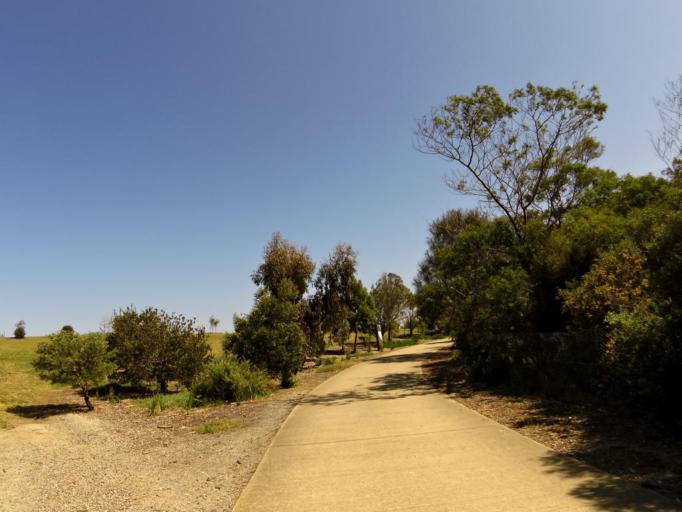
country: AU
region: Victoria
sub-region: Hobsons Bay
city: Altona Meadows
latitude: -37.8807
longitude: 144.7997
